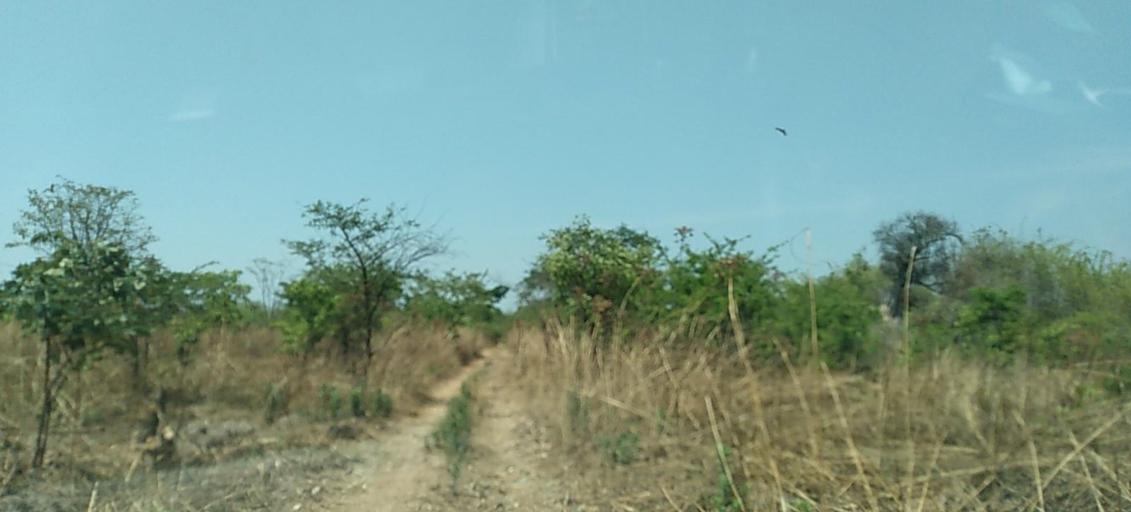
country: ZM
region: Copperbelt
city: Luanshya
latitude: -12.9825
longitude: 28.3288
